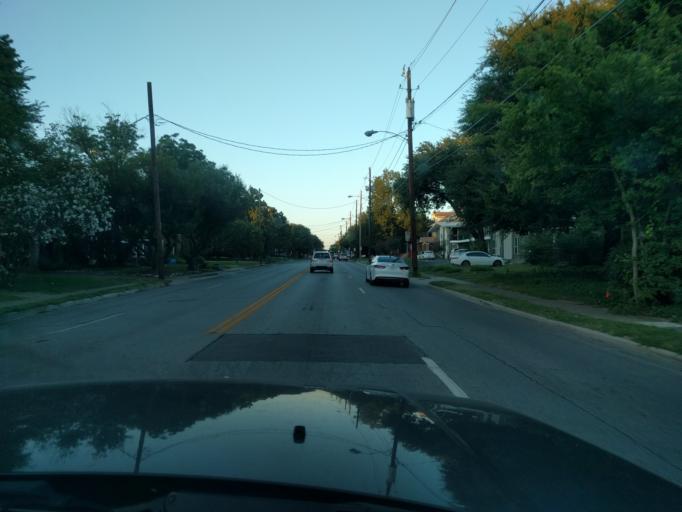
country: US
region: Texas
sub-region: Dallas County
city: Dallas
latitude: 32.7981
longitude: -96.7718
